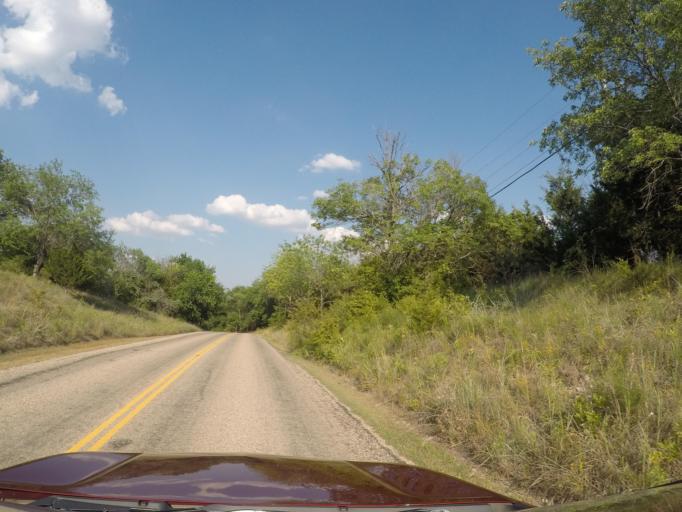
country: US
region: Texas
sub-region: Grayson County
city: Preston
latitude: 33.8105
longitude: -96.6074
